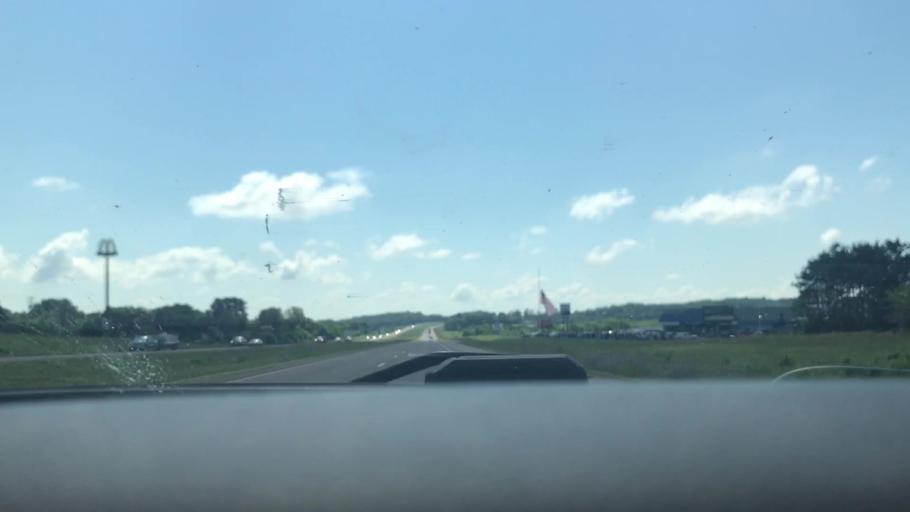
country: US
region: Wisconsin
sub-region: Chippewa County
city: Bloomer
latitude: 45.0990
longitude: -91.5037
